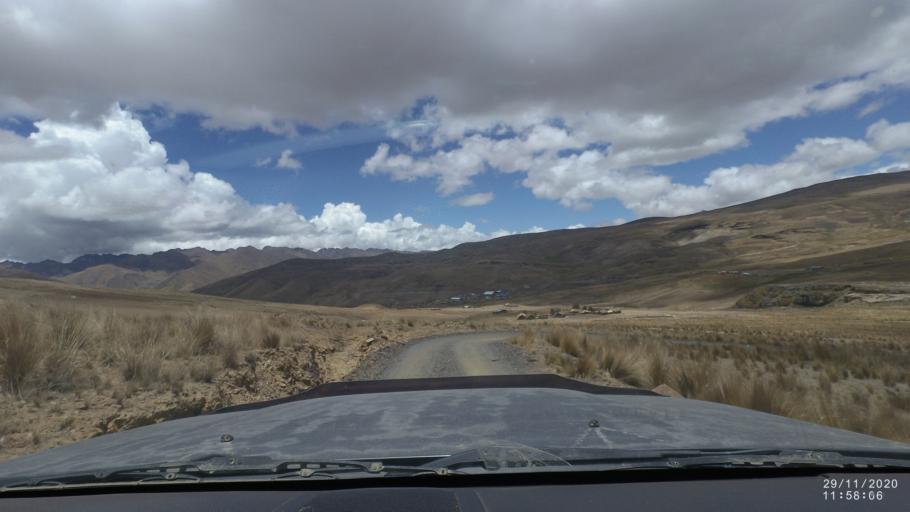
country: BO
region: Cochabamba
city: Cochabamba
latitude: -17.1566
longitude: -66.2754
